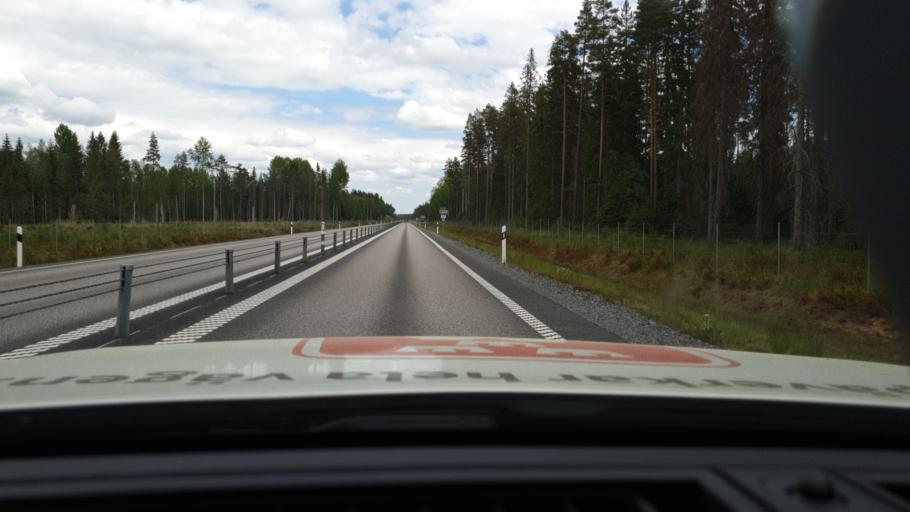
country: SE
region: Uppsala
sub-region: Heby Kommun
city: Tarnsjo
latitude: 60.0583
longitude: 16.8960
